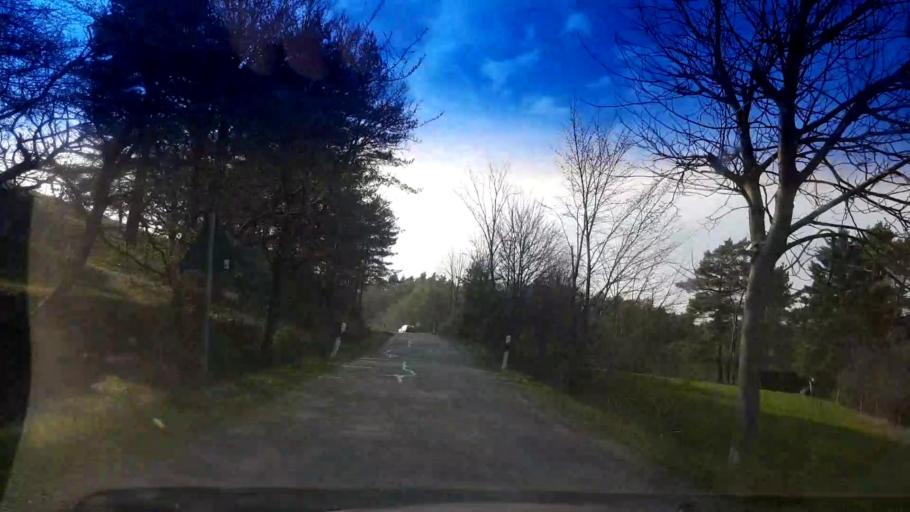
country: DE
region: Bavaria
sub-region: Upper Franconia
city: Neudrossenfeld
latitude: 50.0519
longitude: 11.5082
